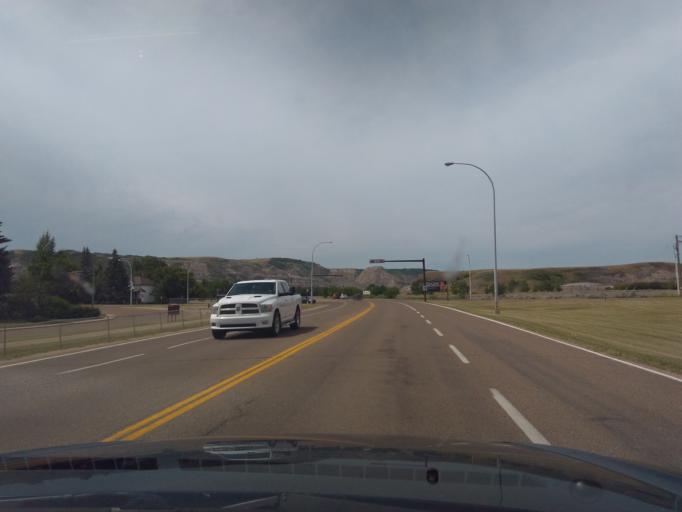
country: CA
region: Alberta
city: Three Hills
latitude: 51.4690
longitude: -112.7459
